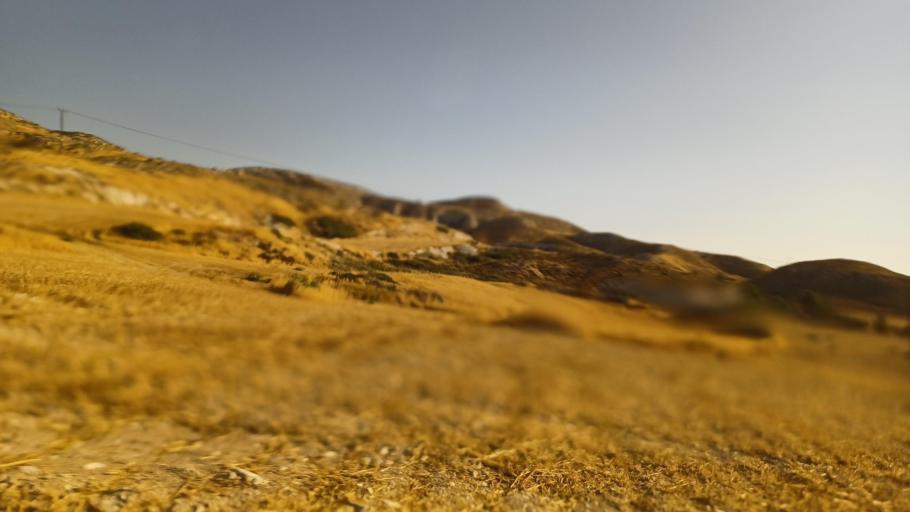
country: CY
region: Larnaka
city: Troulloi
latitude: 35.0263
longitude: 33.5796
